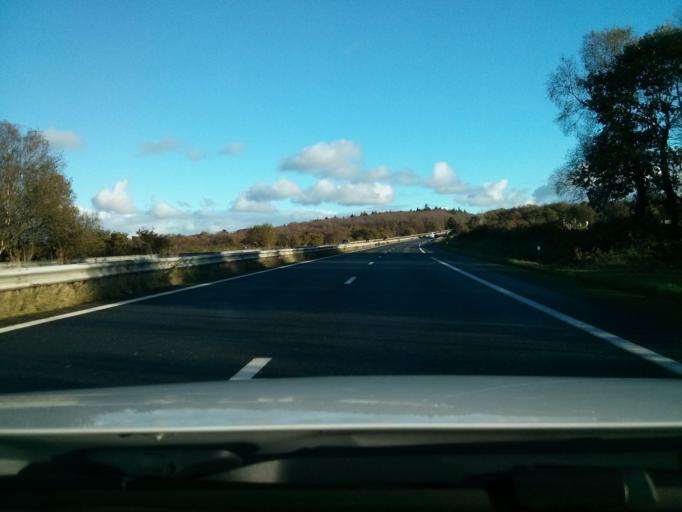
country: FR
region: Brittany
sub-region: Departement du Finistere
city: Plouigneau
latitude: 48.5758
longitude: -3.6959
